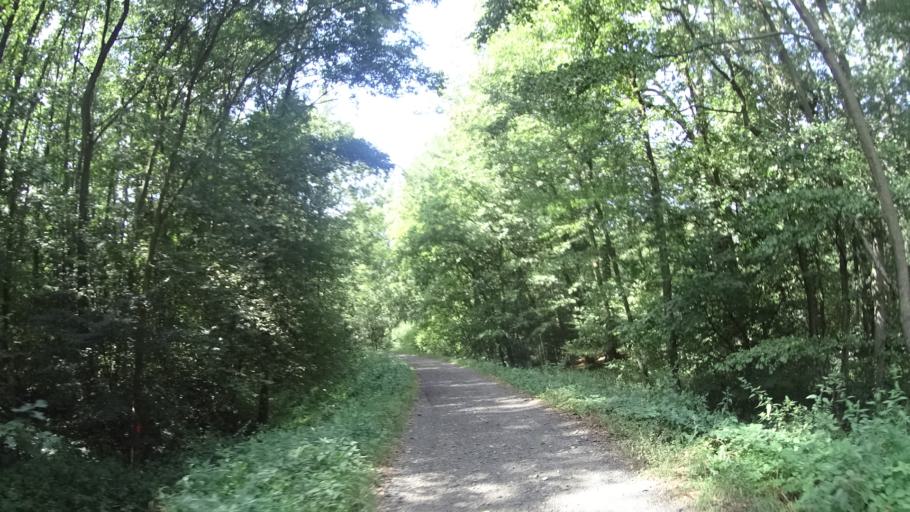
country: CZ
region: Olomoucky
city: Skrben
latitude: 49.6736
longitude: 17.1718
